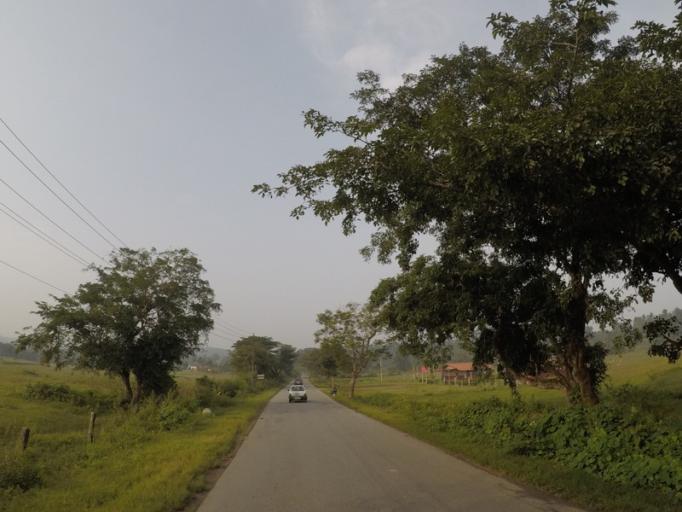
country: IN
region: Karnataka
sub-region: Chikmagalur
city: Mudigere
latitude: 13.2507
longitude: 75.6609
